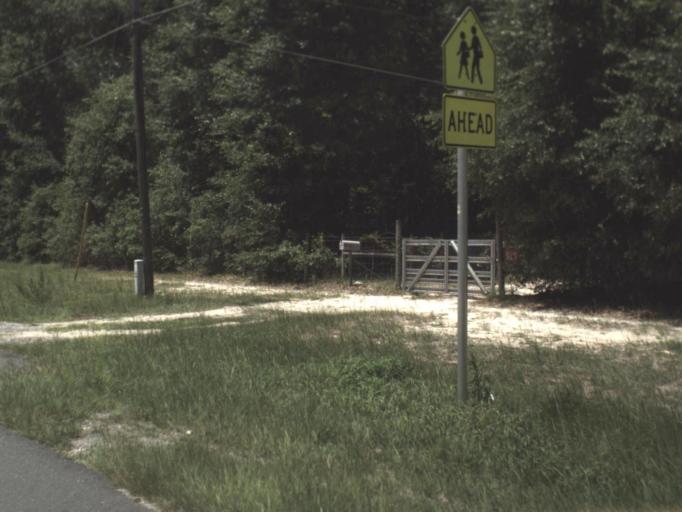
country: US
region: Florida
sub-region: Alachua County
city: Hawthorne
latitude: 29.6334
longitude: -82.0305
